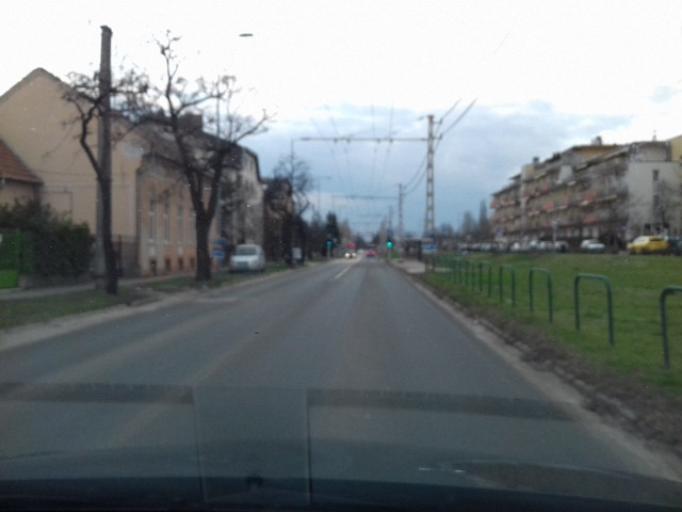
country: HU
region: Budapest
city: Budapest XIV. keruelet
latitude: 47.5209
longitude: 19.1240
